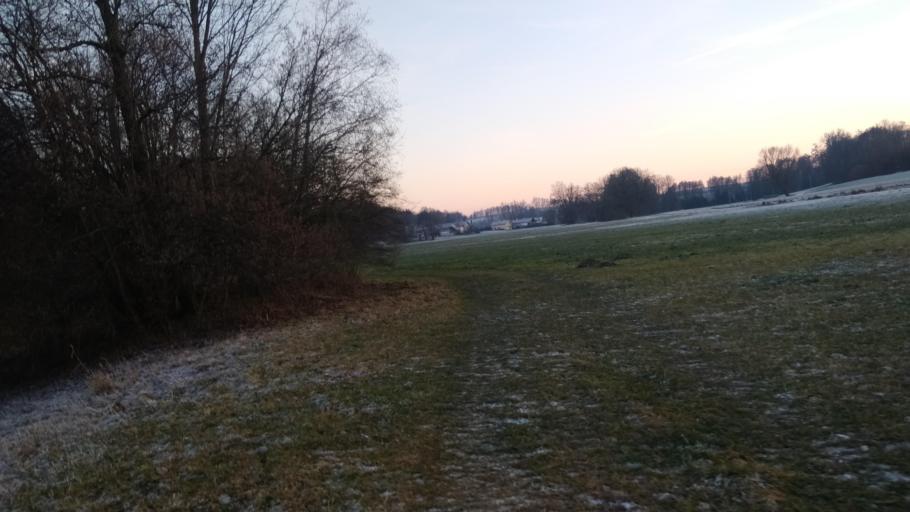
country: DE
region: Bavaria
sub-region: Upper Bavaria
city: Obertaufkirchen
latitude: 48.2611
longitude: 12.2710
